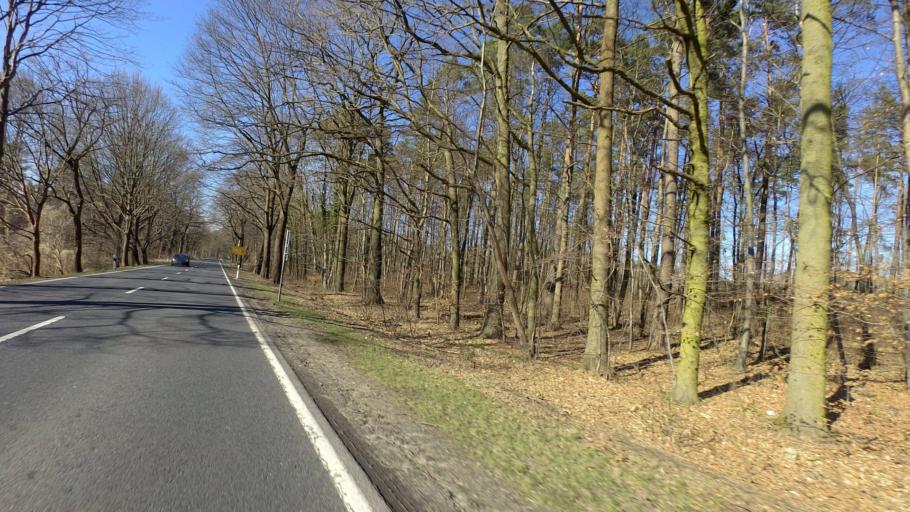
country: DE
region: Brandenburg
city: Chorin
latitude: 52.8975
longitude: 13.8908
